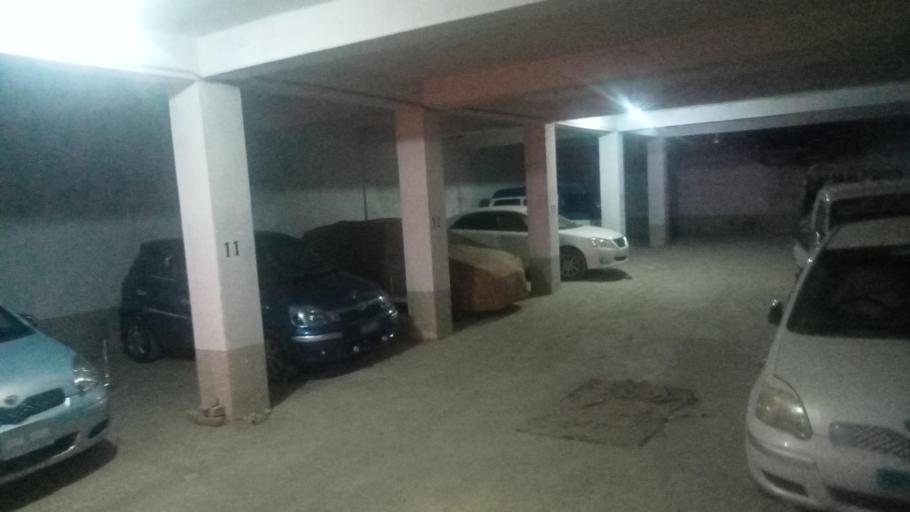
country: PK
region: Khyber Pakhtunkhwa
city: Mingora
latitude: 34.7823
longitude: 72.3615
